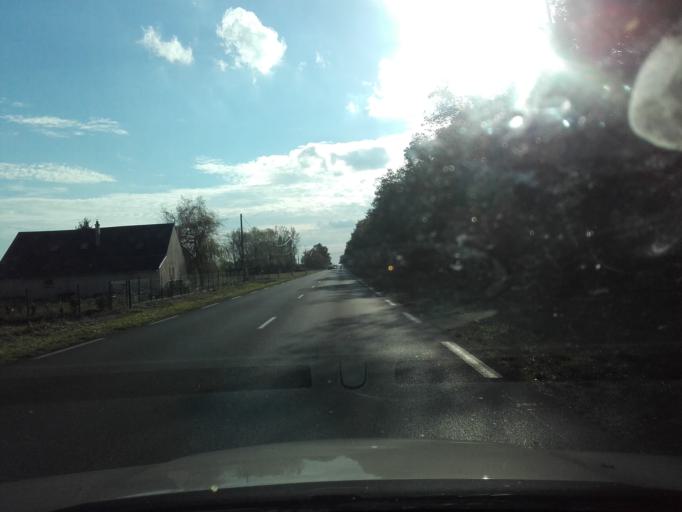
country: FR
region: Centre
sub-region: Departement d'Indre-et-Loire
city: Monnaie
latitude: 47.4869
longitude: 0.7714
